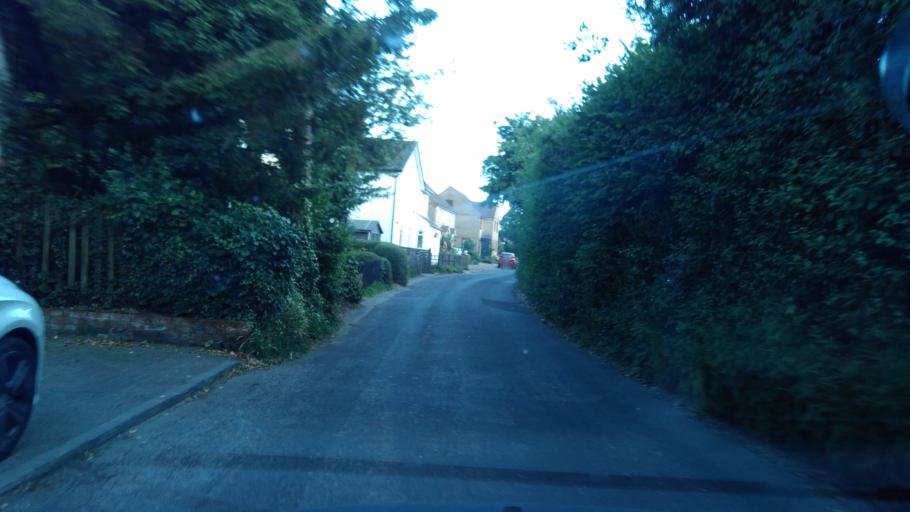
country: GB
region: England
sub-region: Kent
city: Dunkirk
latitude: 51.2776
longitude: 0.9400
